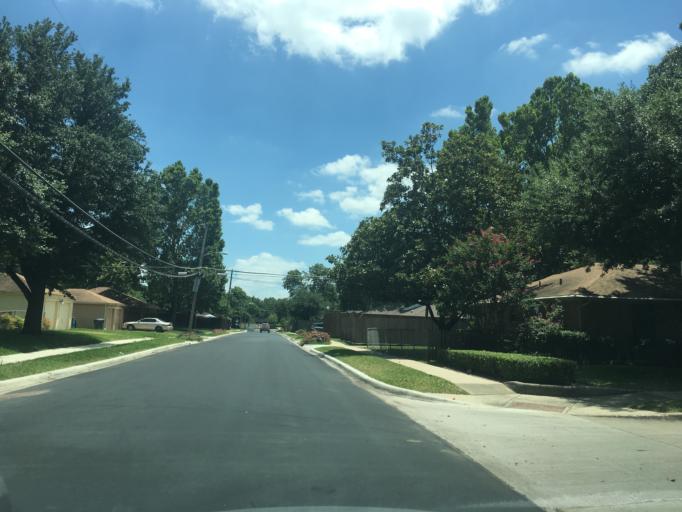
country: US
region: Texas
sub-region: Dallas County
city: Garland
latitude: 32.8325
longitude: -96.6637
